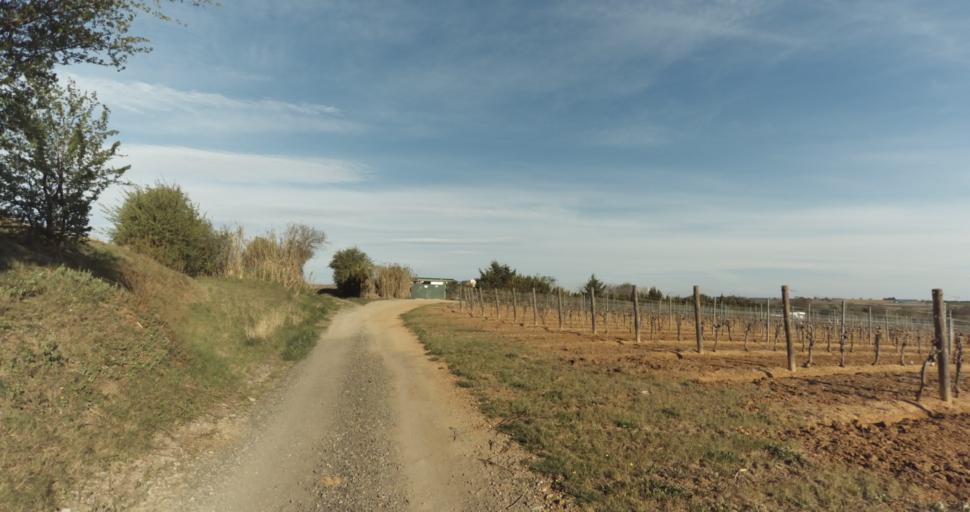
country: FR
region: Languedoc-Roussillon
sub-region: Departement de l'Herault
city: Marseillan
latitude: 43.3700
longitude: 3.5126
